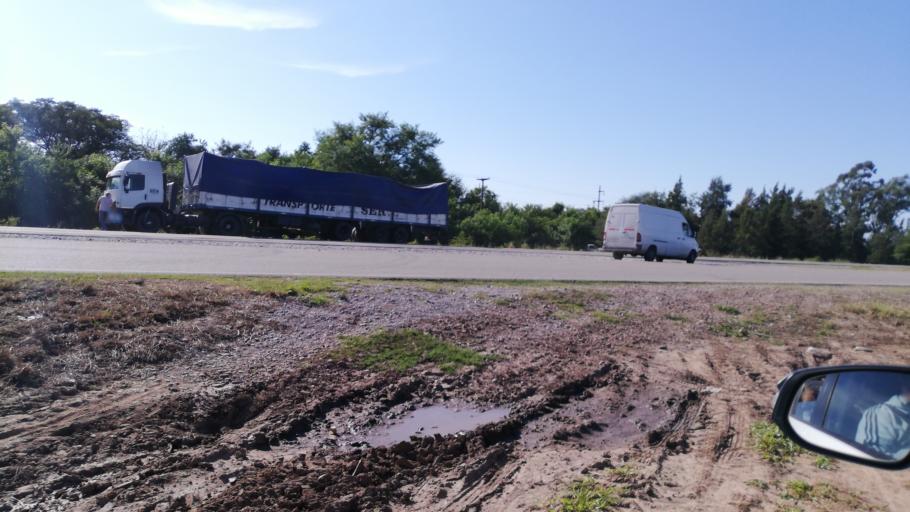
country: AR
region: Jujuy
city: La Mendieta
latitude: -24.3934
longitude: -65.0865
